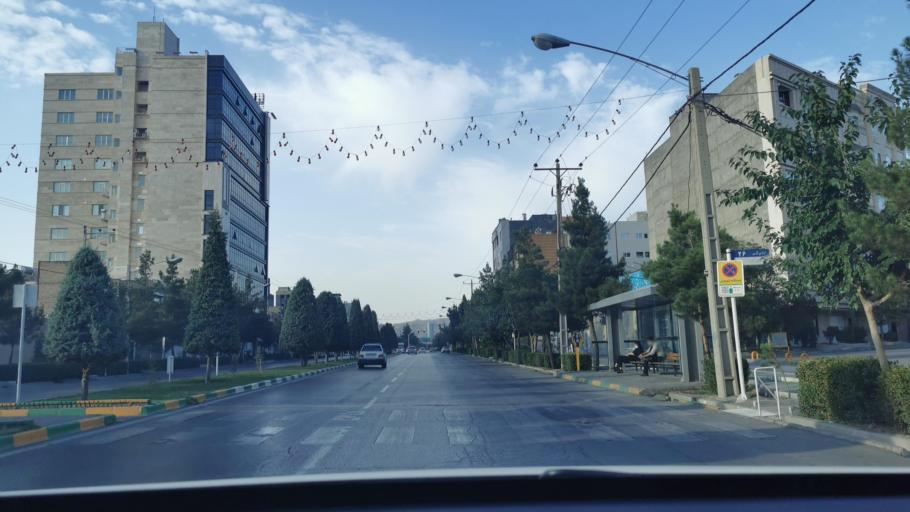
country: IR
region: Razavi Khorasan
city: Mashhad
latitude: 36.3539
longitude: 59.5016
